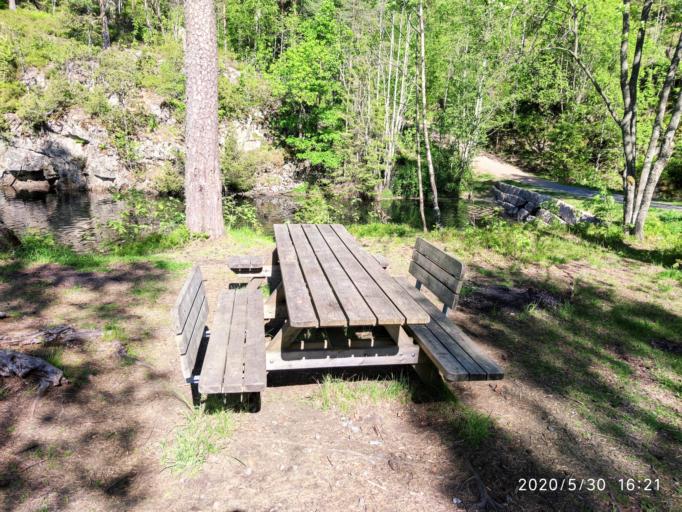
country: NO
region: Buskerud
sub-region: Drammen
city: Drammen
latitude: 59.7570
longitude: 10.2120
